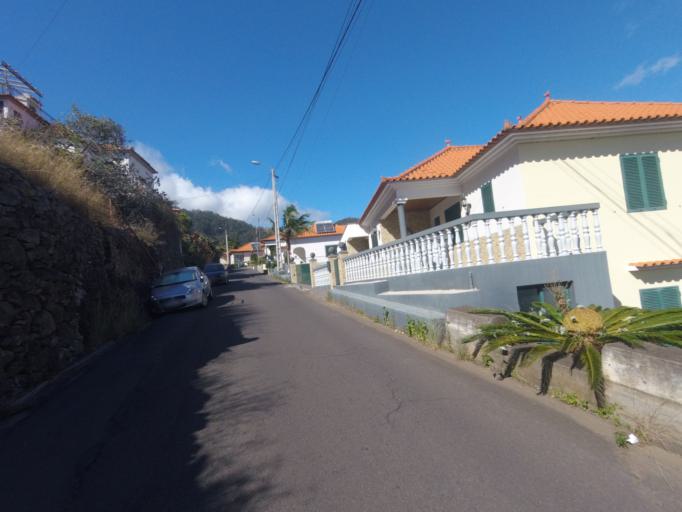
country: PT
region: Madeira
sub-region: Ribeira Brava
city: Campanario
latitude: 32.6727
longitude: -17.0318
